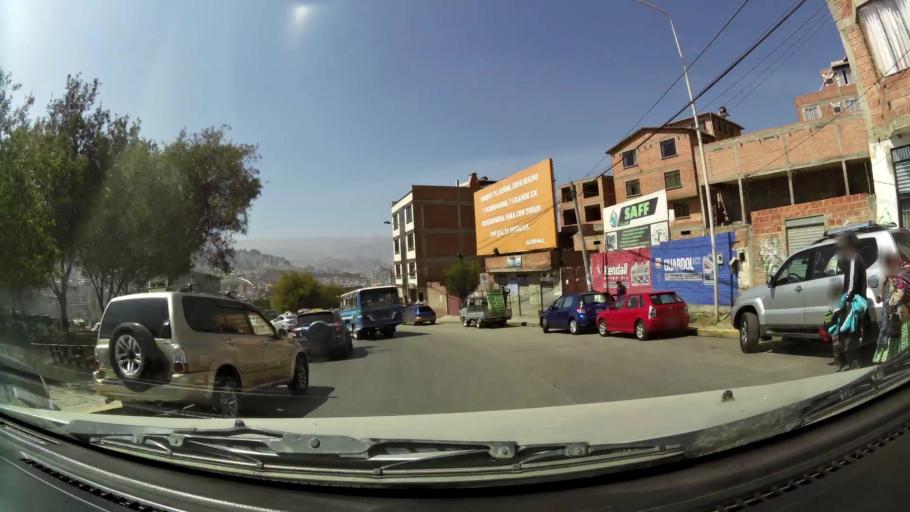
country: BO
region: La Paz
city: La Paz
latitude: -16.5238
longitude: -68.1218
